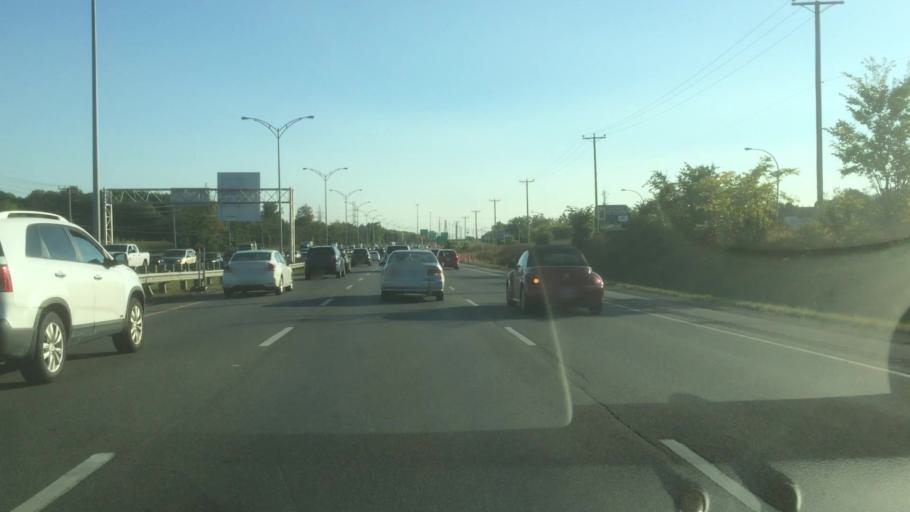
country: CA
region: Quebec
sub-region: Laurentides
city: Boisbriand
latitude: 45.6099
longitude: -73.8549
